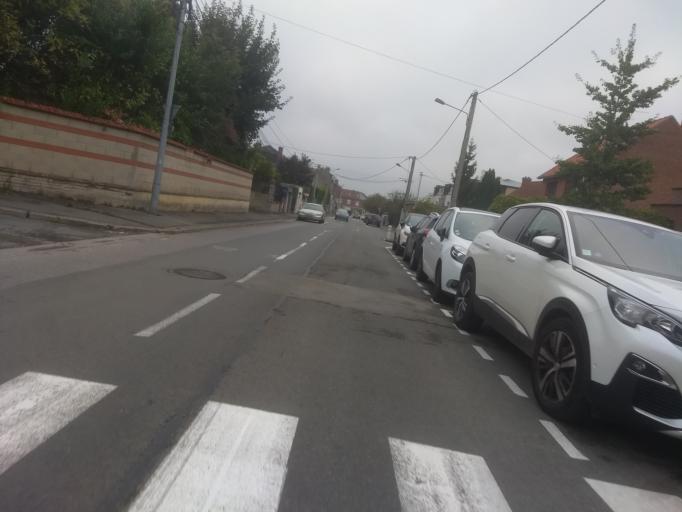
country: FR
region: Nord-Pas-de-Calais
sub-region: Departement du Pas-de-Calais
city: Arras
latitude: 50.2873
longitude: 2.7936
